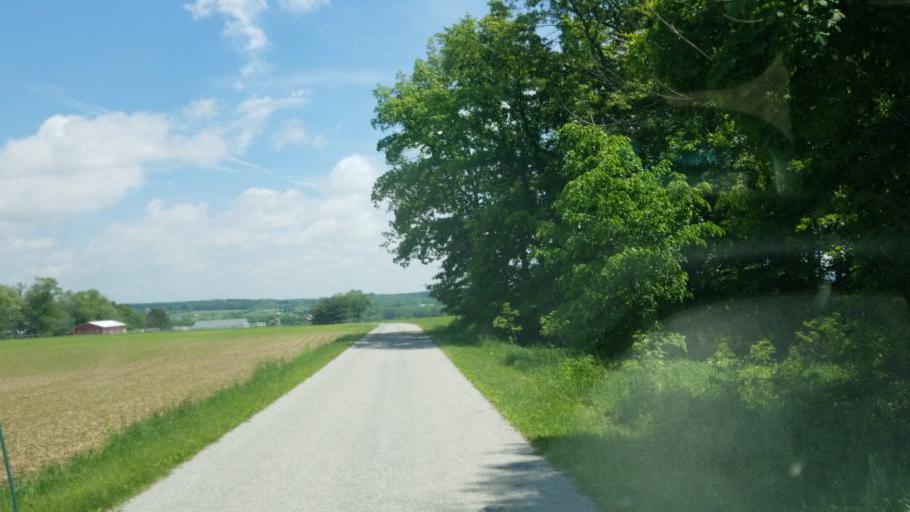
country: US
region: Ohio
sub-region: Wayne County
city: West Salem
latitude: 40.8424
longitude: -82.1573
